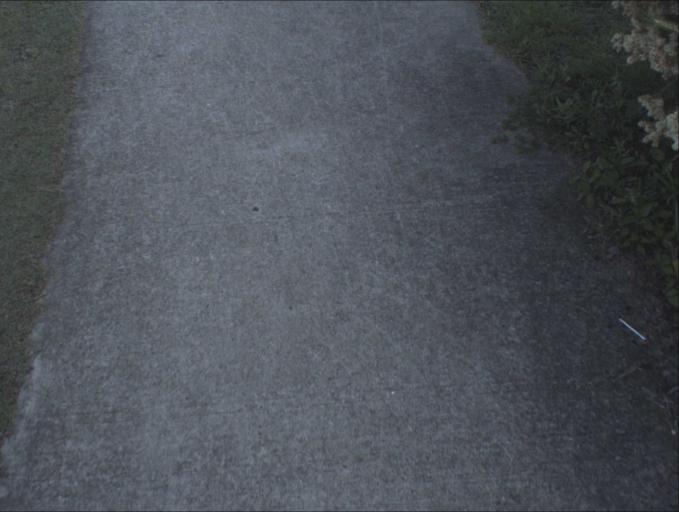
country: AU
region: Queensland
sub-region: Logan
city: North Maclean
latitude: -27.8050
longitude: 152.9549
